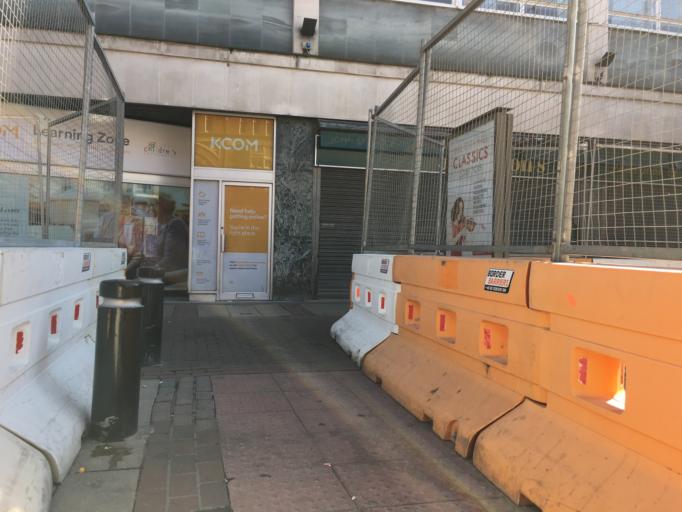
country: GB
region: England
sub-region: City of Kingston upon Hull
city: Hull
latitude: 53.7435
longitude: -0.3420
